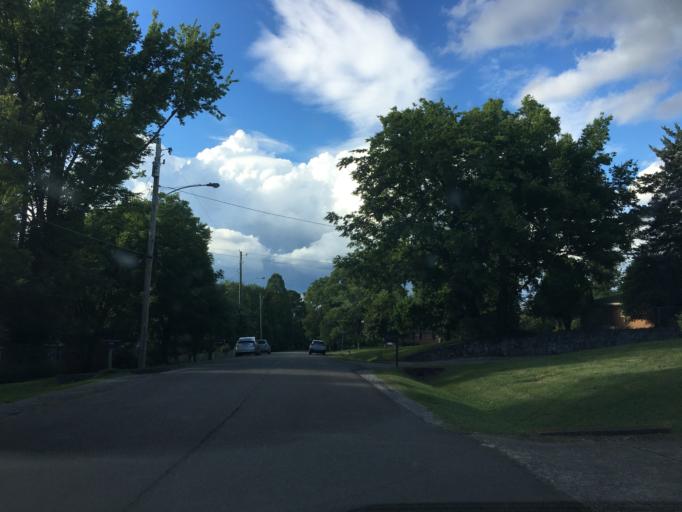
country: US
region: Tennessee
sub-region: Davidson County
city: Oak Hill
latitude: 36.0634
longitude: -86.7215
